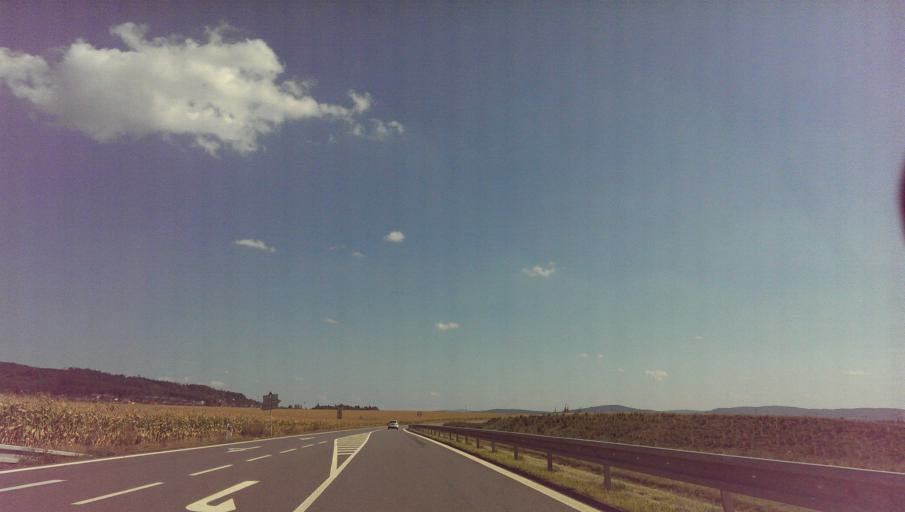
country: CZ
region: Zlin
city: Holesov
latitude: 49.3321
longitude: 17.5951
